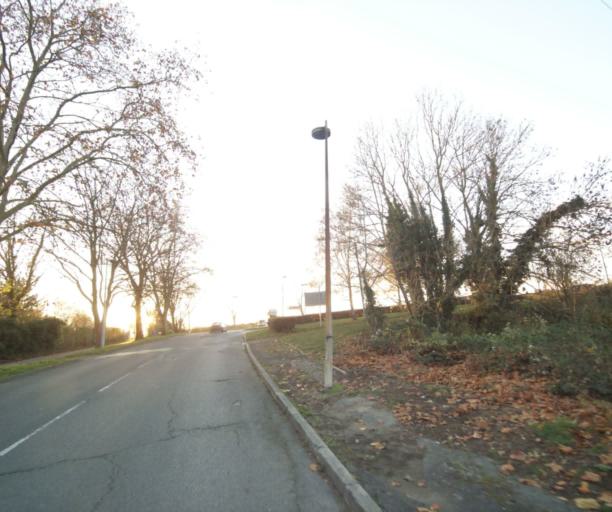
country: FR
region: Ile-de-France
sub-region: Departement du Val-d'Oise
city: Le Thillay
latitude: 48.9986
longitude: 2.4654
